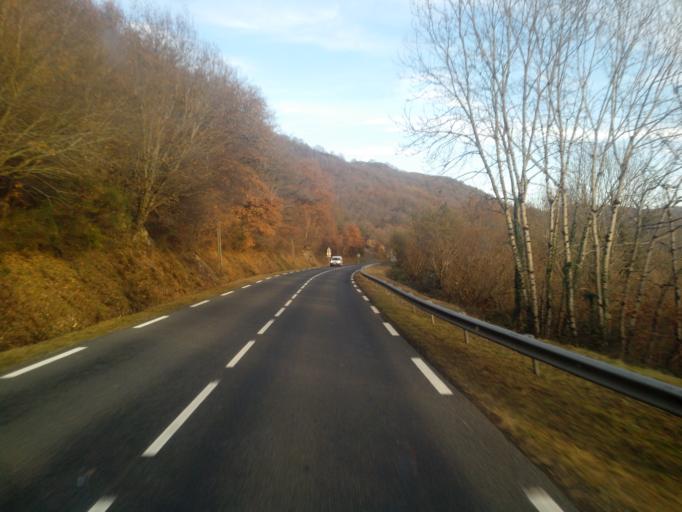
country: FR
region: Auvergne
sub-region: Departement du Cantal
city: Champs-sur-Tarentaine-Marchal
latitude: 45.3396
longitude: 2.5598
